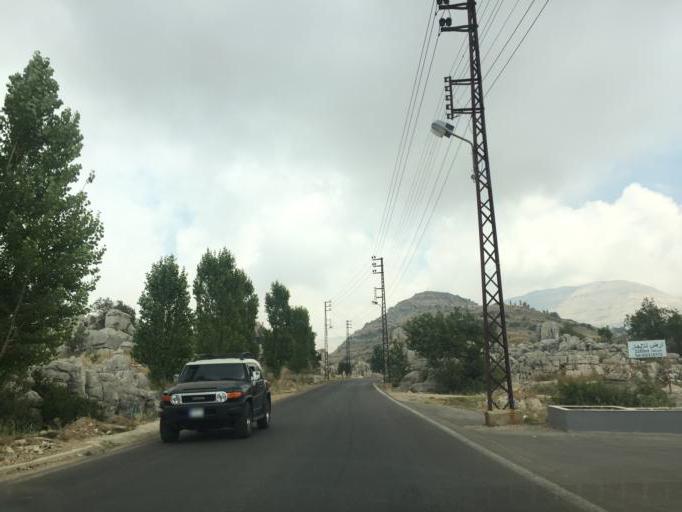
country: LB
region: Beqaa
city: Zahle
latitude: 34.0006
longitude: 35.8039
